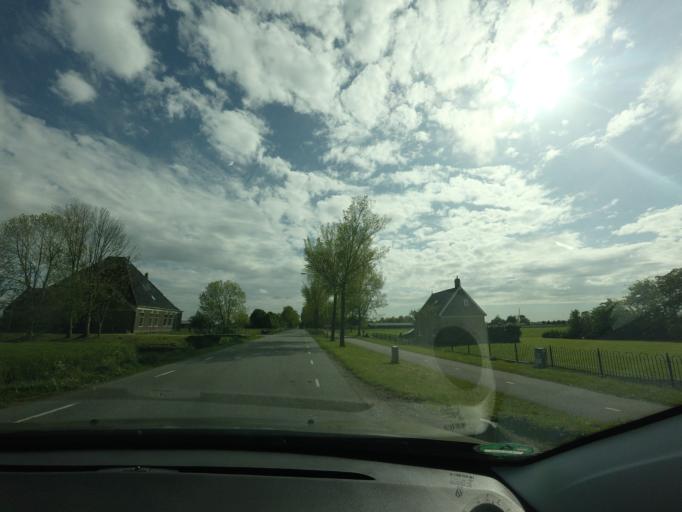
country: NL
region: North Holland
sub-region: Gemeente Beemster
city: Halfweg
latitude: 52.5667
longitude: 4.9239
